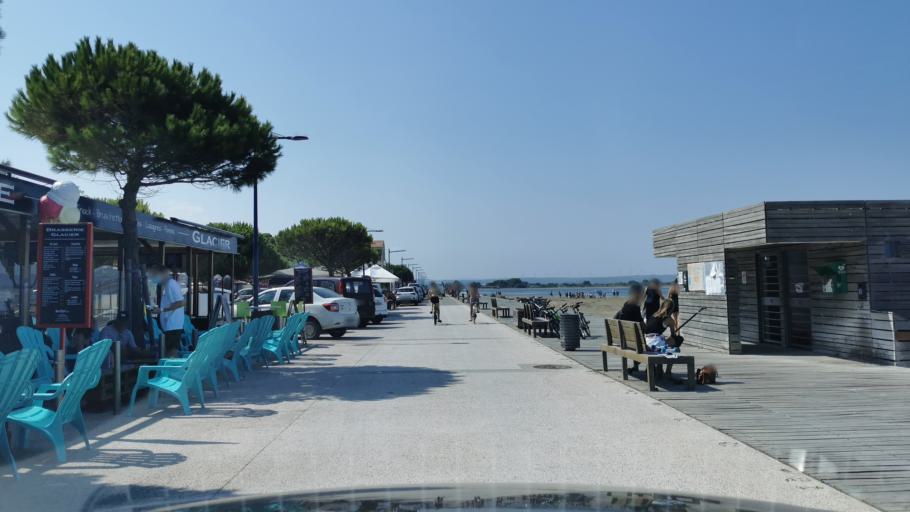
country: FR
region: Languedoc-Roussillon
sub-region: Departement de l'Aude
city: Leucate
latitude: 42.9310
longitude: 3.0385
